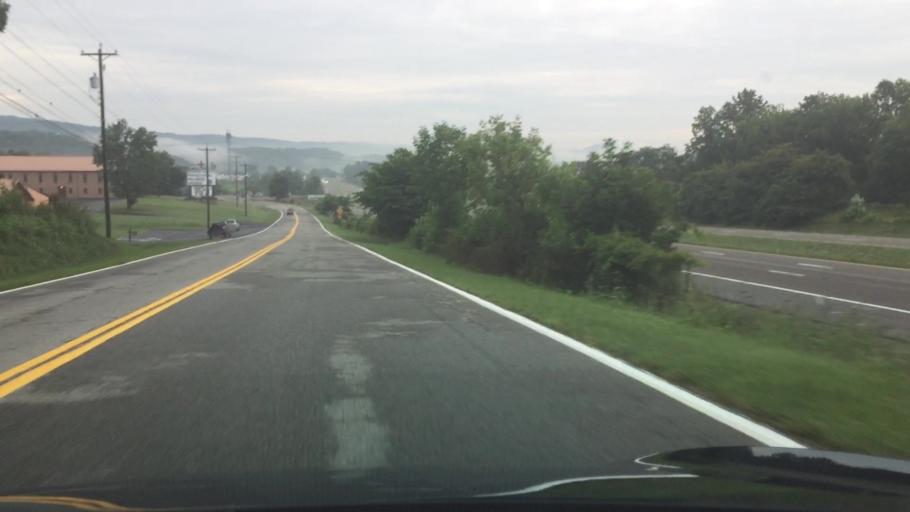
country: US
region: Virginia
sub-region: Pulaski County
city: Pulaski
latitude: 36.9620
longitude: -80.8557
